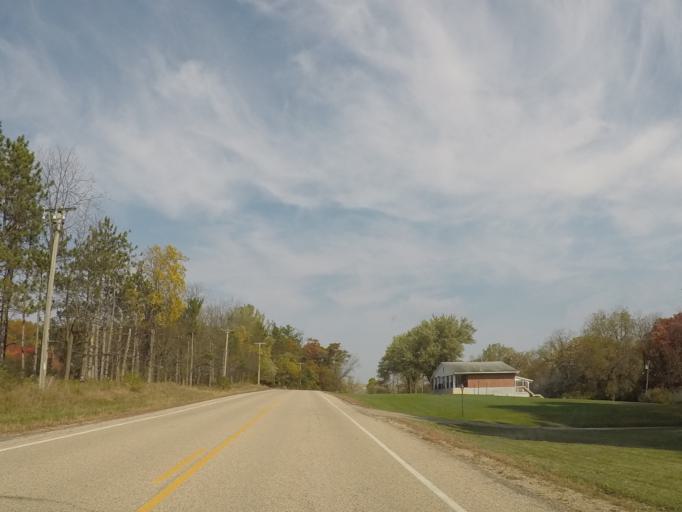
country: US
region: Wisconsin
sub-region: Dane County
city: Cross Plains
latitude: 43.0286
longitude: -89.6214
